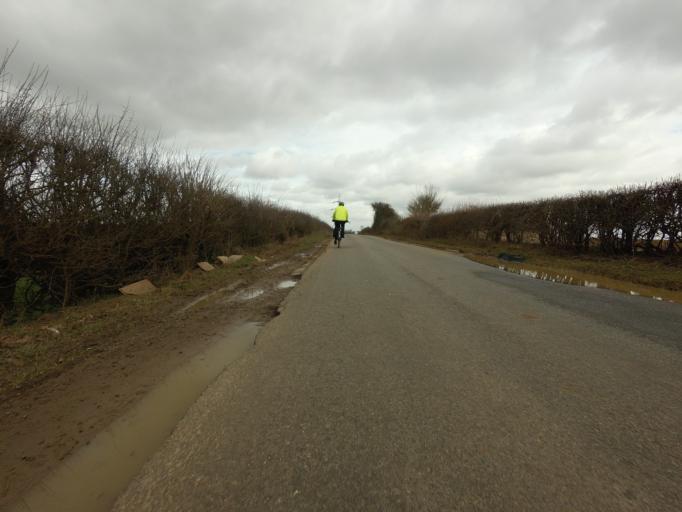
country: GB
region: England
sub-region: Lincolnshire
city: Grantham
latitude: 52.8864
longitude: -0.6616
